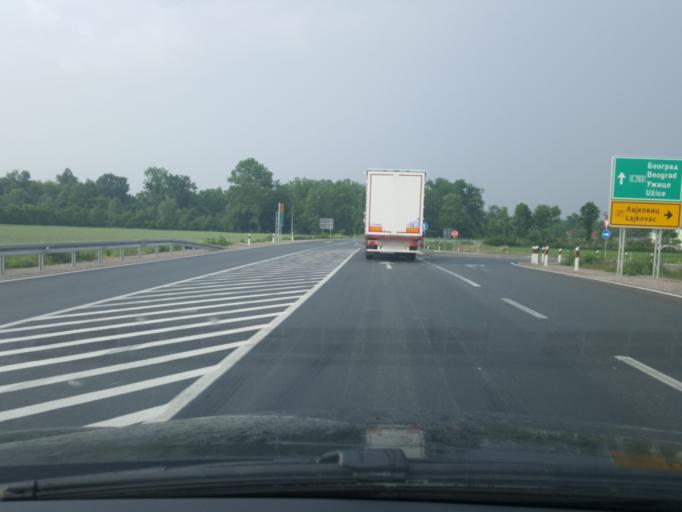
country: RS
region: Central Serbia
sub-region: Kolubarski Okrug
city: Lajkovac
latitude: 44.3583
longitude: 20.1132
